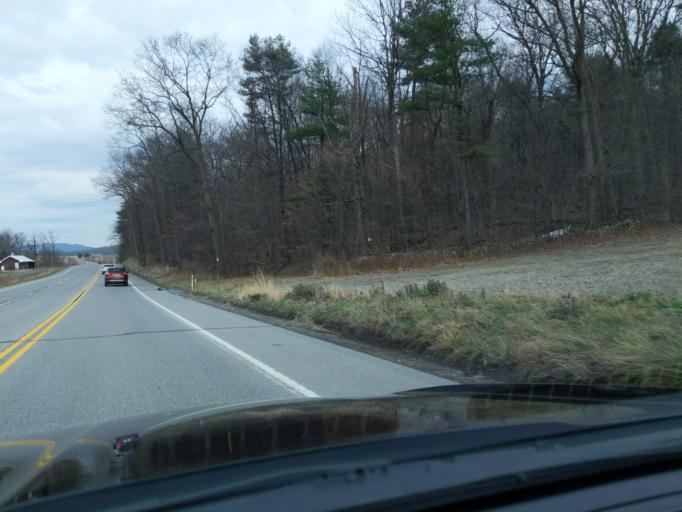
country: US
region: Pennsylvania
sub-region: Blair County
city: Williamsburg
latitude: 40.5130
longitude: -78.2130
